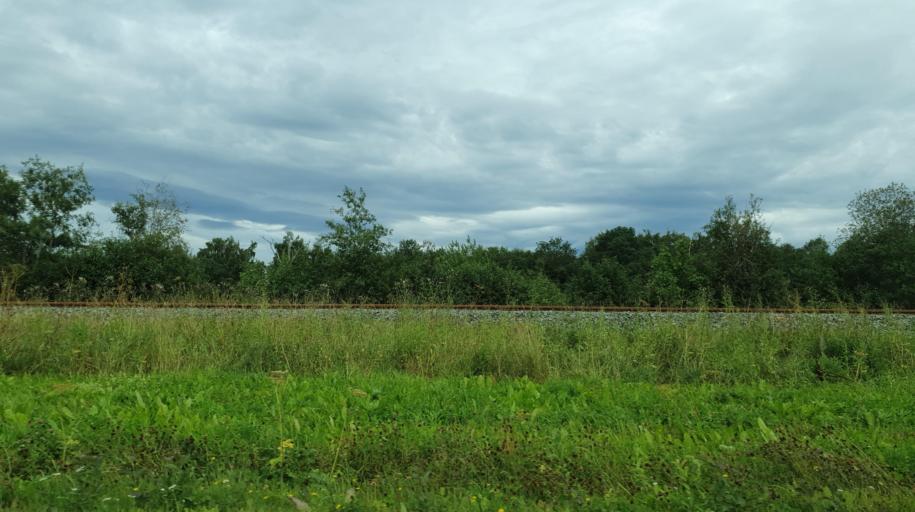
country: NO
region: Nord-Trondelag
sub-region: Stjordal
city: Stjordalshalsen
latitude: 63.4461
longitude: 10.9617
